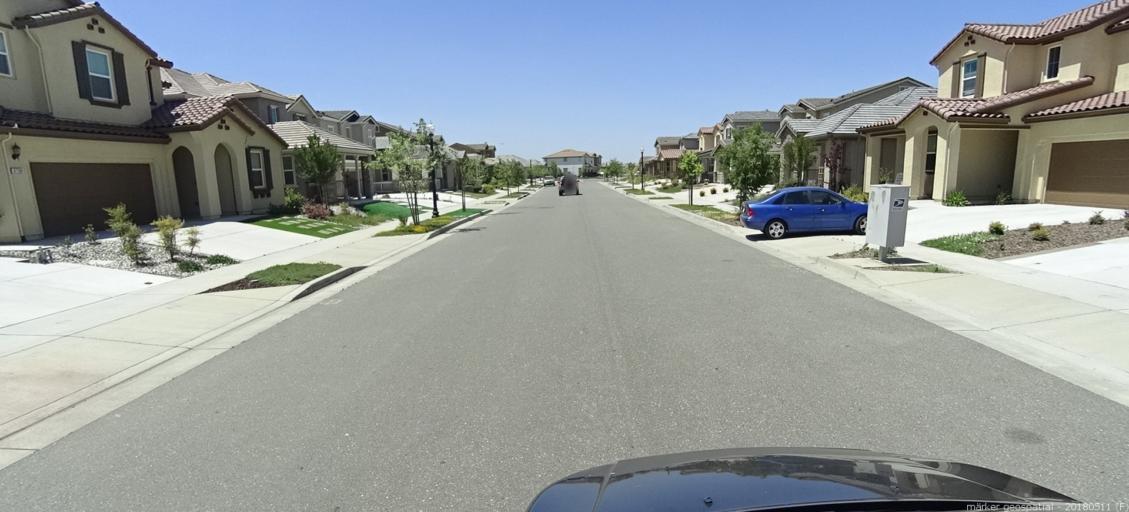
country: US
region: California
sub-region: Yolo County
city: West Sacramento
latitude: 38.6459
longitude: -121.5450
